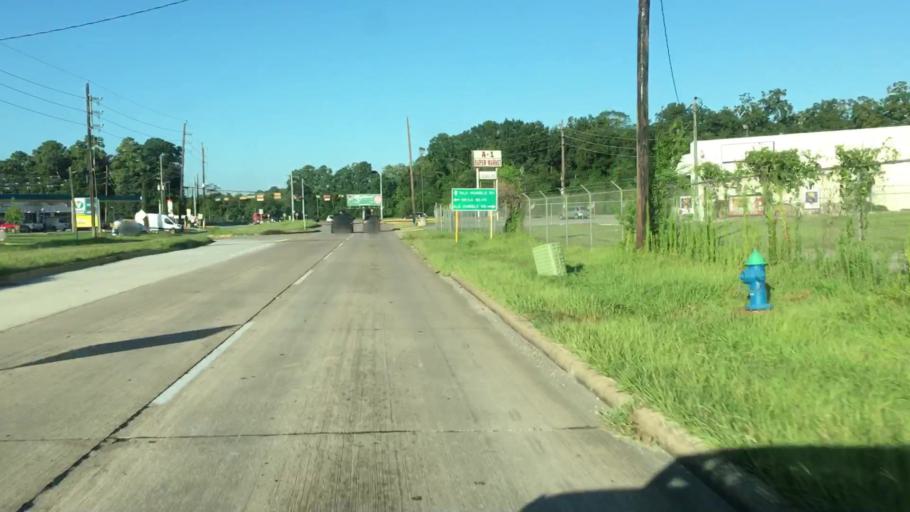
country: US
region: Texas
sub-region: Harris County
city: Humble
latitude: 29.9568
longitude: -95.2648
